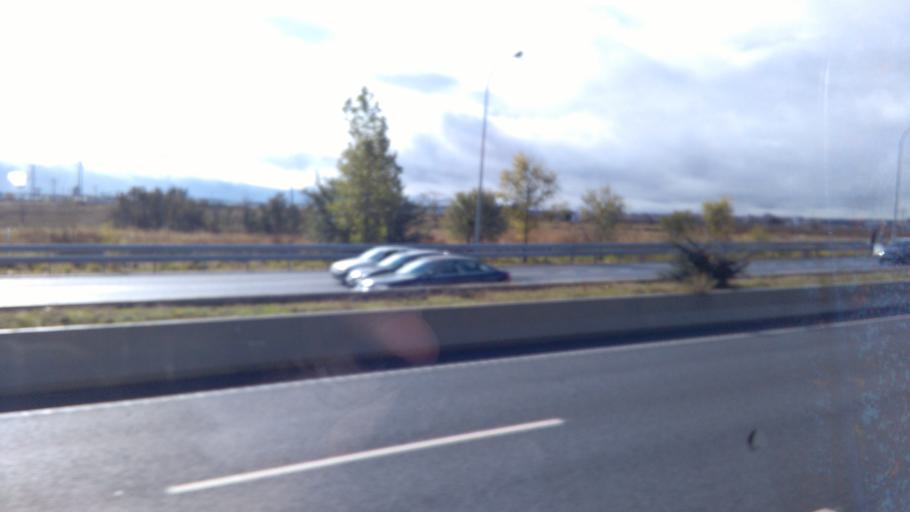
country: ES
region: Madrid
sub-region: Provincia de Madrid
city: Carabanchel
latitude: 40.3643
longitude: -3.7270
